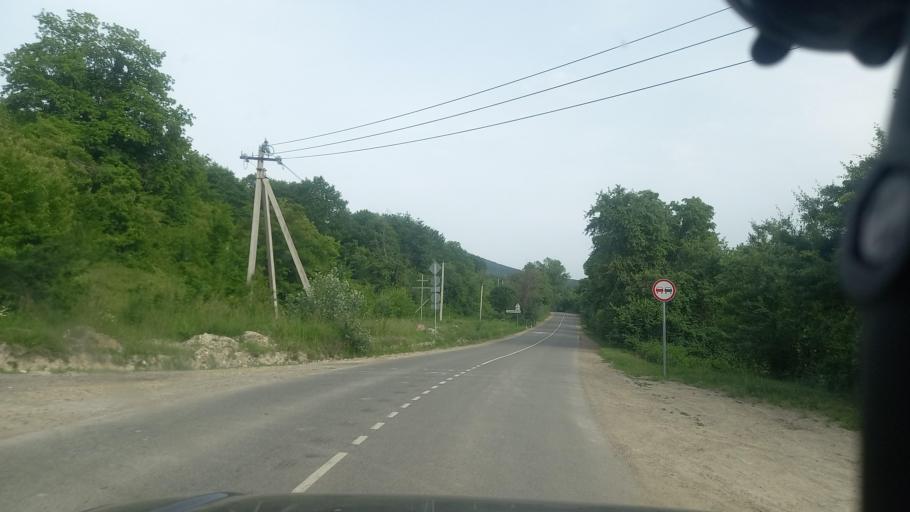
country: RU
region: Krasnodarskiy
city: Goryachiy Klyuch
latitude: 44.6061
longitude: 39.0357
